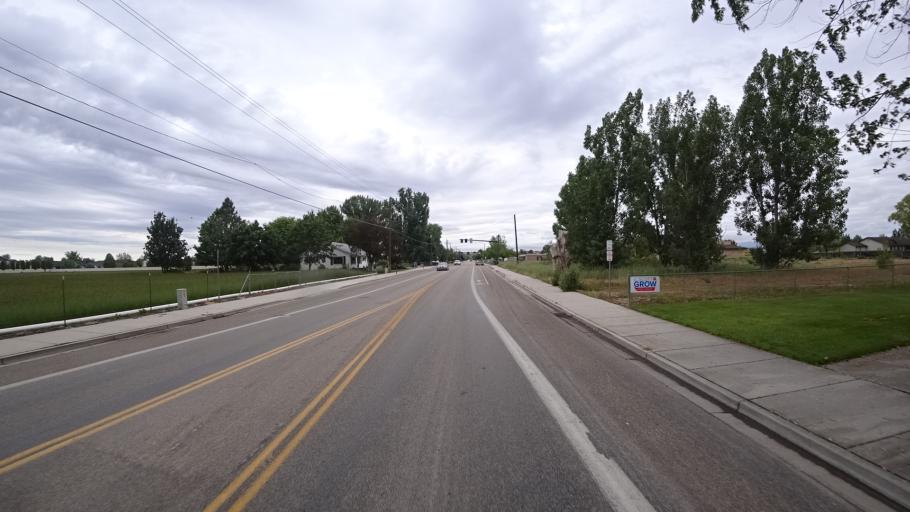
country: US
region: Idaho
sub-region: Ada County
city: Star
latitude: 43.6967
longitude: -116.4933
